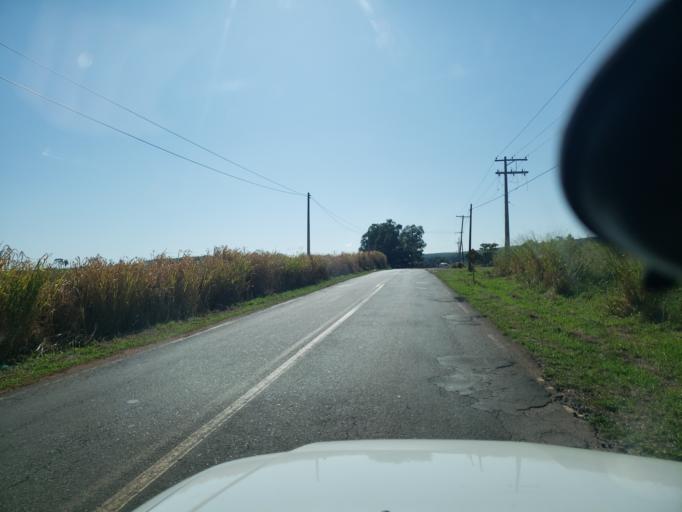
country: BR
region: Sao Paulo
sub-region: Moji-Guacu
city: Mogi-Gaucu
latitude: -22.3375
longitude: -46.8844
